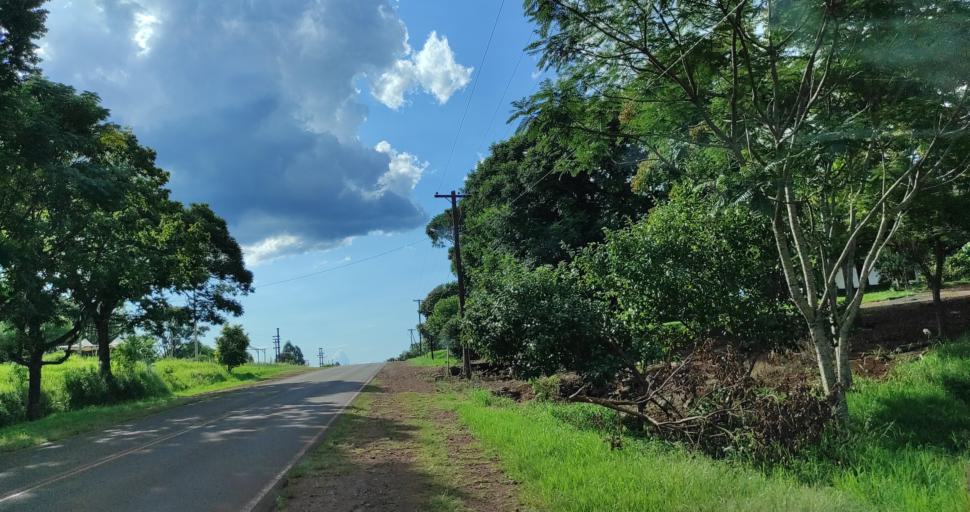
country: AR
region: Misiones
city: San Vicente
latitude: -26.3442
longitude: -54.1556
